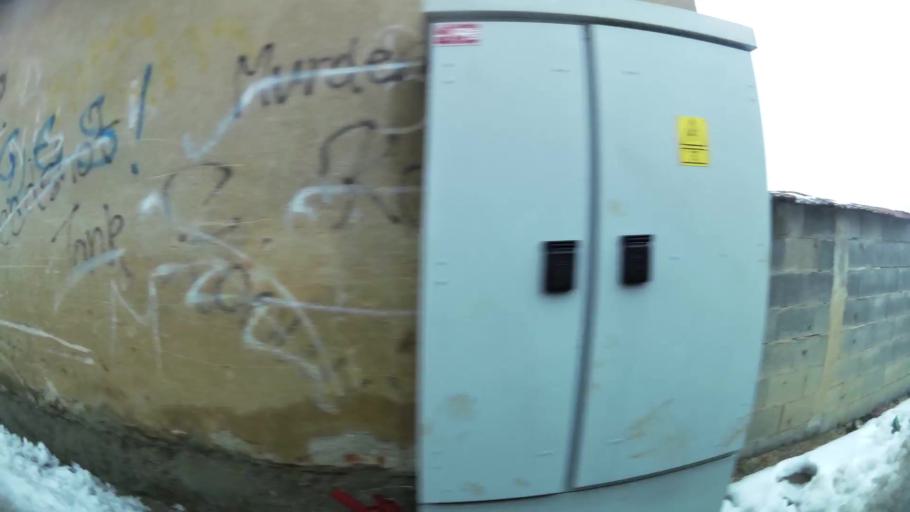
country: XK
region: Pristina
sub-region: Komuna e Prishtines
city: Pristina
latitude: 42.6417
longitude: 21.1461
